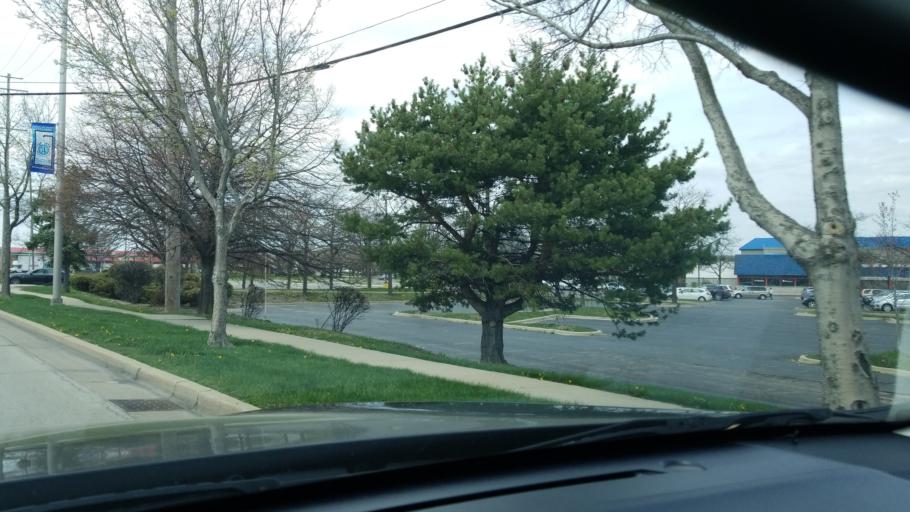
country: US
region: Illinois
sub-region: Cook County
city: Elk Grove Village
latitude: 42.0436
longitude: -87.9810
